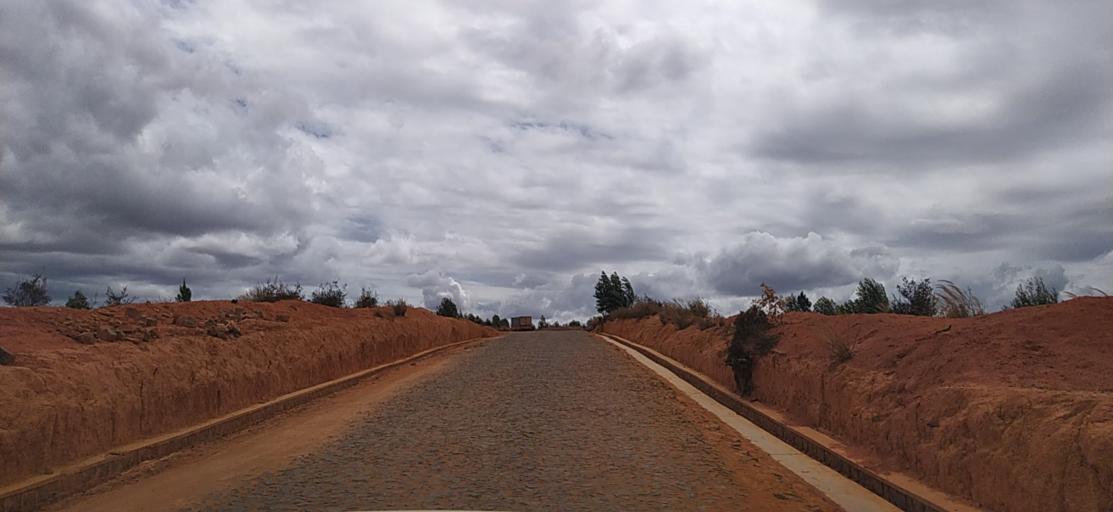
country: MG
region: Alaotra Mangoro
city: Ambatondrazaka
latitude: -18.0576
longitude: 48.2552
